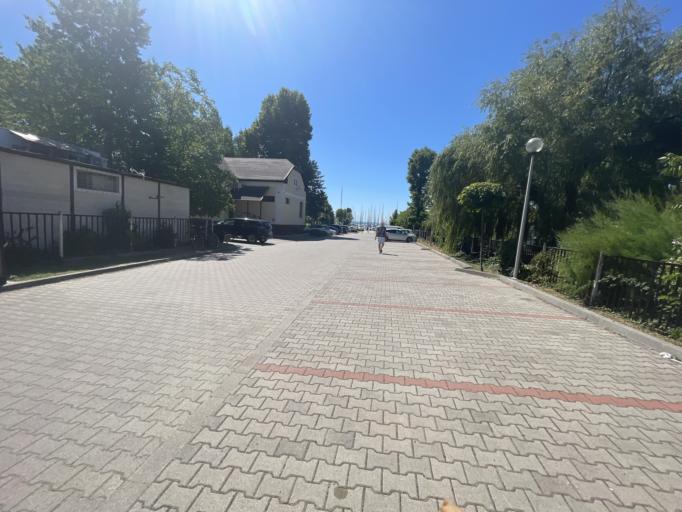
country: HU
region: Veszprem
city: Csopak
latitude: 46.9851
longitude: 17.9786
